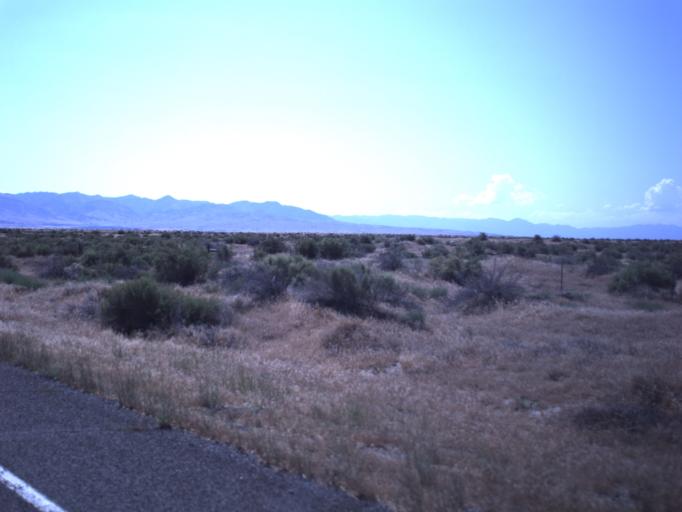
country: US
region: Utah
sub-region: Millard County
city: Delta
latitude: 39.4802
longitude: -112.5083
